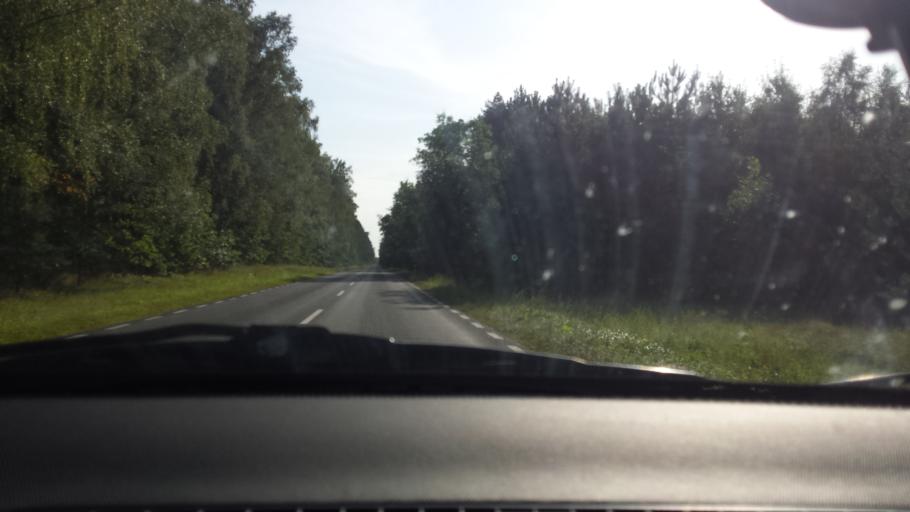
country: PL
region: Masovian Voivodeship
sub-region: Powiat makowski
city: Makow Mazowiecki
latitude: 52.9006
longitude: 21.1440
